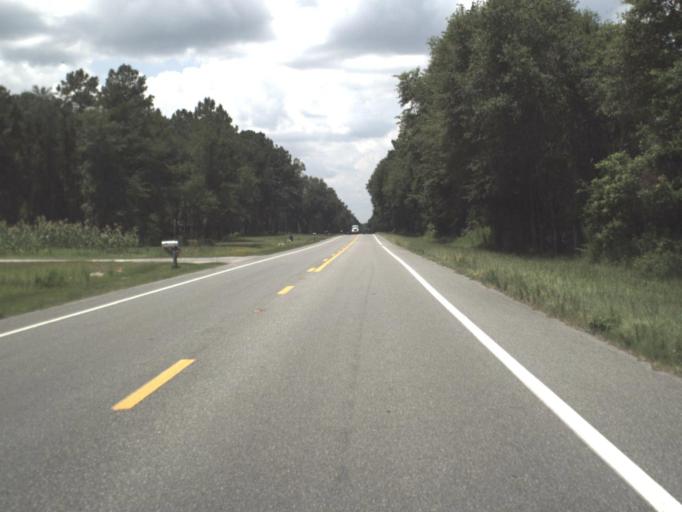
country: US
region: Florida
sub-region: Columbia County
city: Five Points
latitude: 30.2697
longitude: -82.6919
